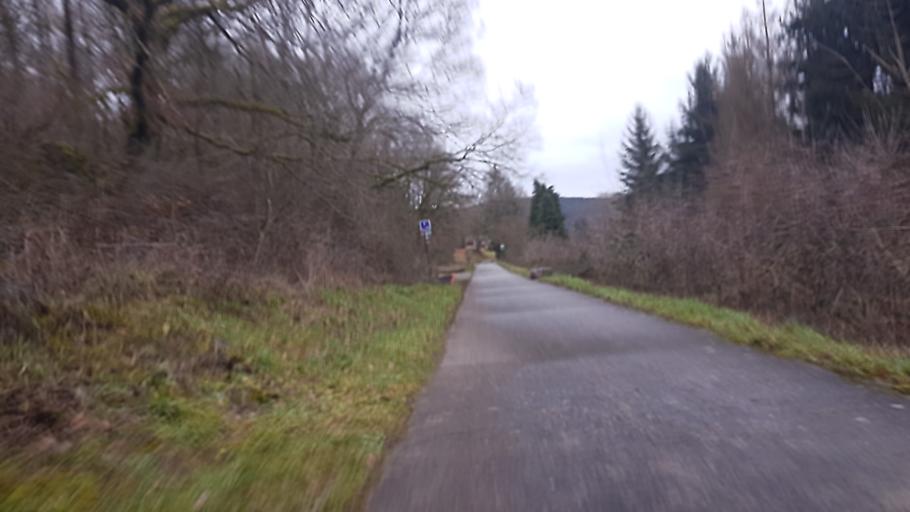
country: BE
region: Wallonia
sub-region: Province de Namur
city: Couvin
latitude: 50.0678
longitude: 4.6039
